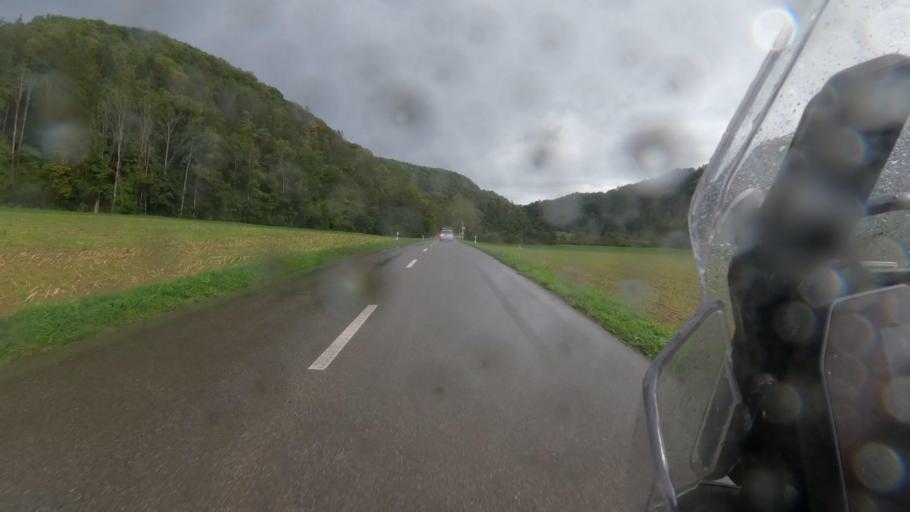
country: CH
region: Schaffhausen
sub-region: Bezirk Oberklettgau
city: Neunkirch
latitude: 47.6491
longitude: 8.5133
